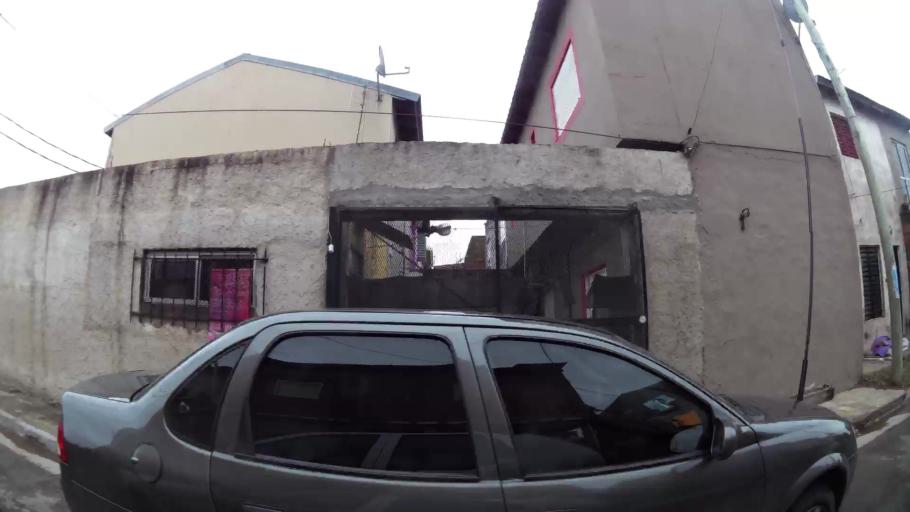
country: AR
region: Buenos Aires
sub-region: Partido de Lanus
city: Lanus
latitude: -34.7337
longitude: -58.3708
